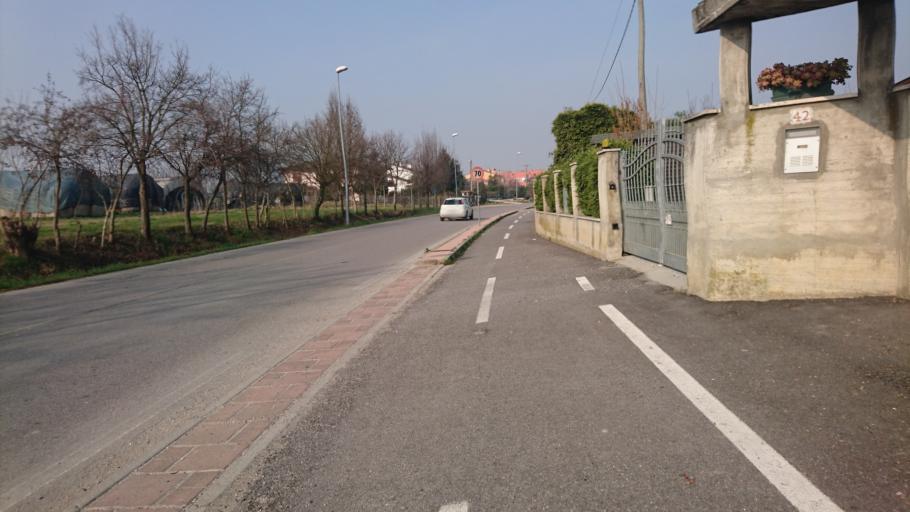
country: IT
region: Veneto
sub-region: Provincia di Padova
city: Veggiano
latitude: 45.4545
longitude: 11.7020
